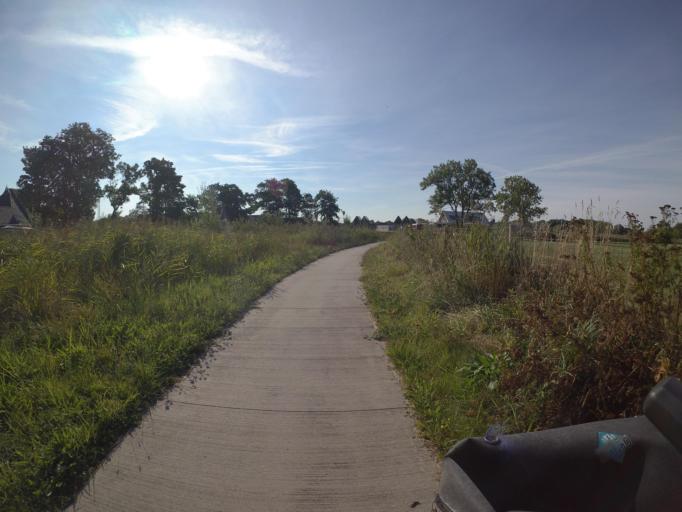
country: NL
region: Friesland
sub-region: Gemeente Dongeradeel
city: Dokkum
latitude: 53.3226
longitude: 5.9793
